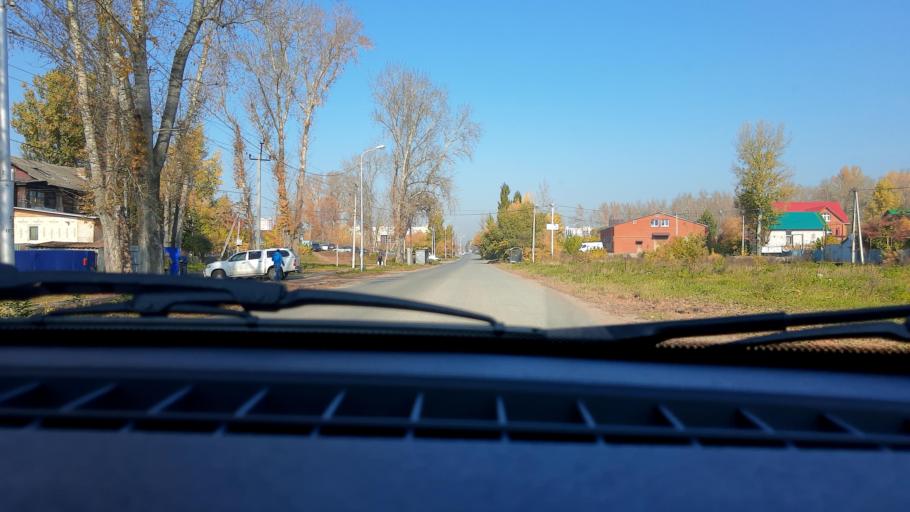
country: RU
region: Bashkortostan
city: Mikhaylovka
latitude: 54.7730
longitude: 55.8936
